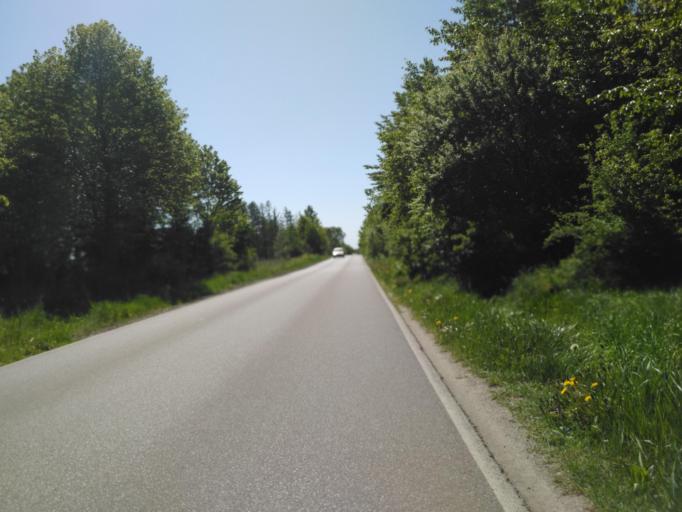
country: PL
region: Subcarpathian Voivodeship
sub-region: Krosno
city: Krosno
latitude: 49.6721
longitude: 21.7898
